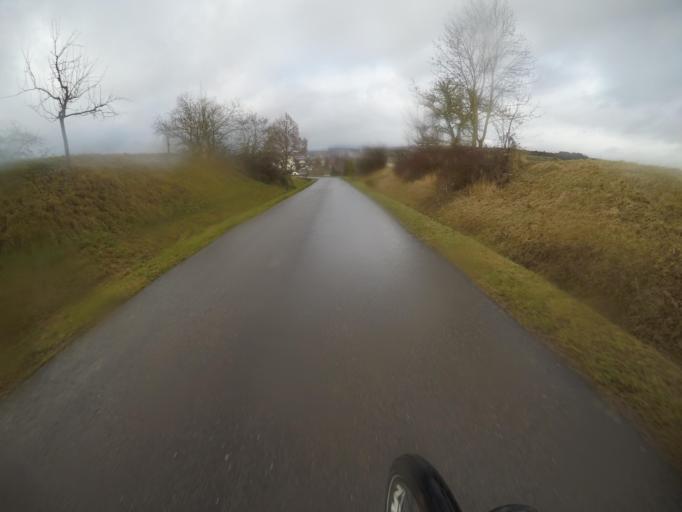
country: DE
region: Baden-Wuerttemberg
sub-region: Regierungsbezirk Stuttgart
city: Eberdingen
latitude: 48.9121
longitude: 8.9870
